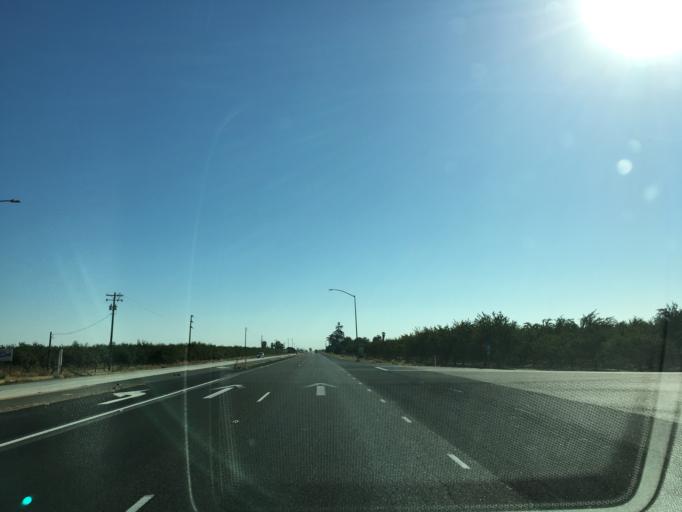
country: US
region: California
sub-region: Madera County
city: Chowchilla
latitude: 37.0834
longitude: -120.2925
